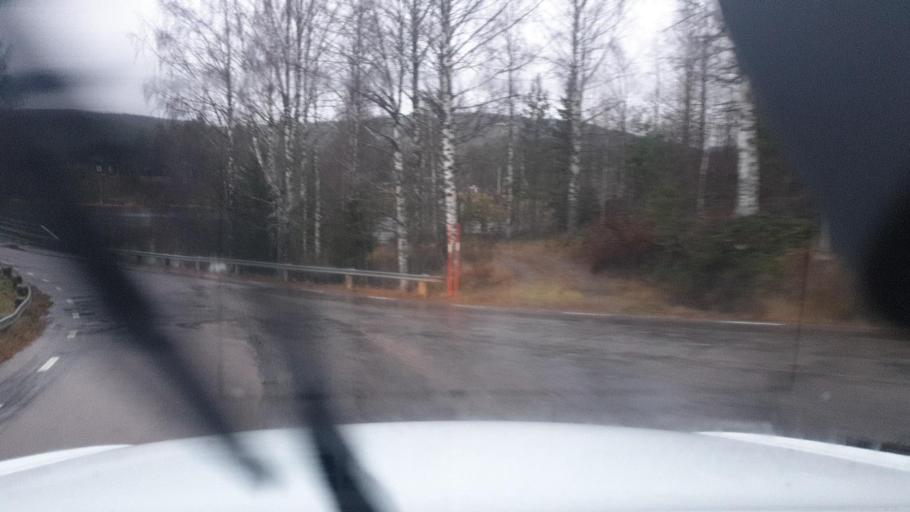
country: SE
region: Vaermland
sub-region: Torsby Kommun
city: Torsby
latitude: 60.1879
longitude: 12.6710
